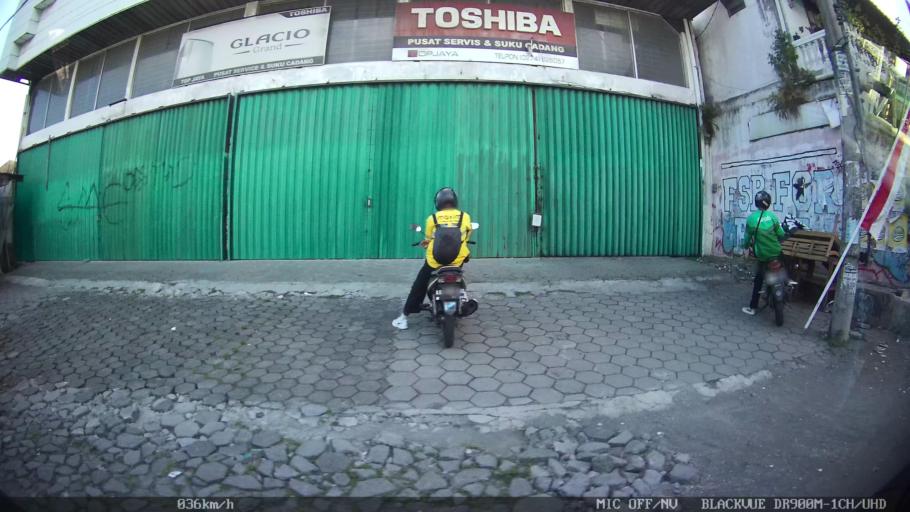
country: ID
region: Daerah Istimewa Yogyakarta
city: Yogyakarta
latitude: -7.7816
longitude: 110.3501
